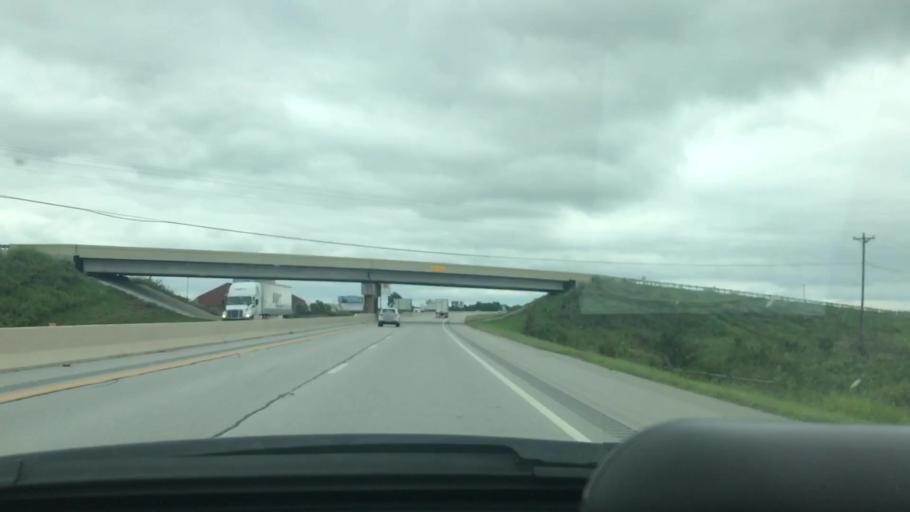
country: US
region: Oklahoma
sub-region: Ottawa County
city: Miami
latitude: 36.8847
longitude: -94.8397
